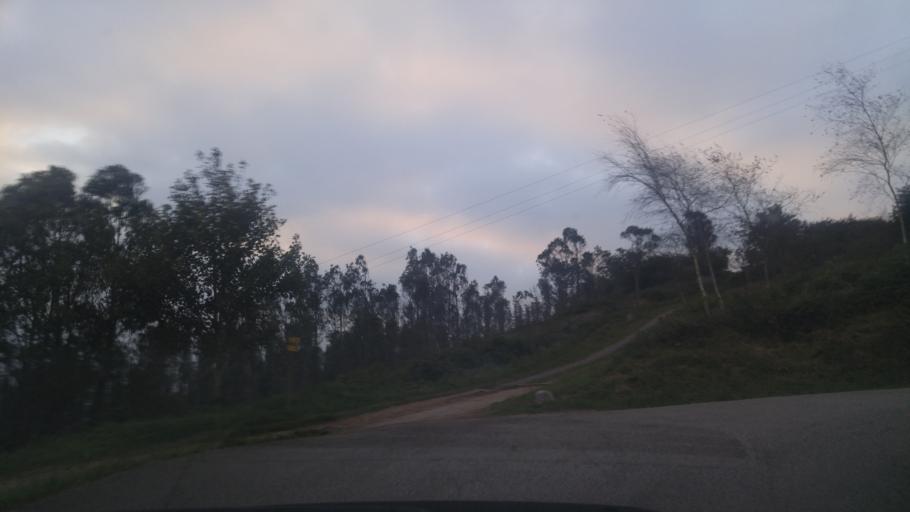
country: ES
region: Asturias
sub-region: Province of Asturias
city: Oviedo
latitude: 43.3845
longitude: -5.8613
